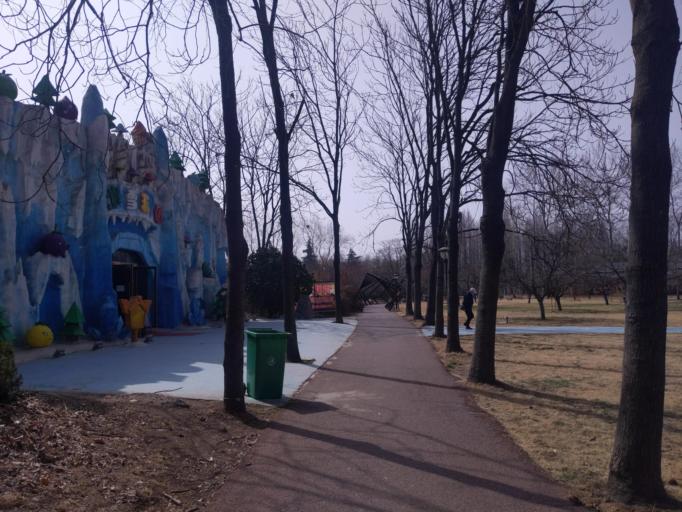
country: CN
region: Henan Sheng
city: Puyang
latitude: 35.7770
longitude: 114.9629
